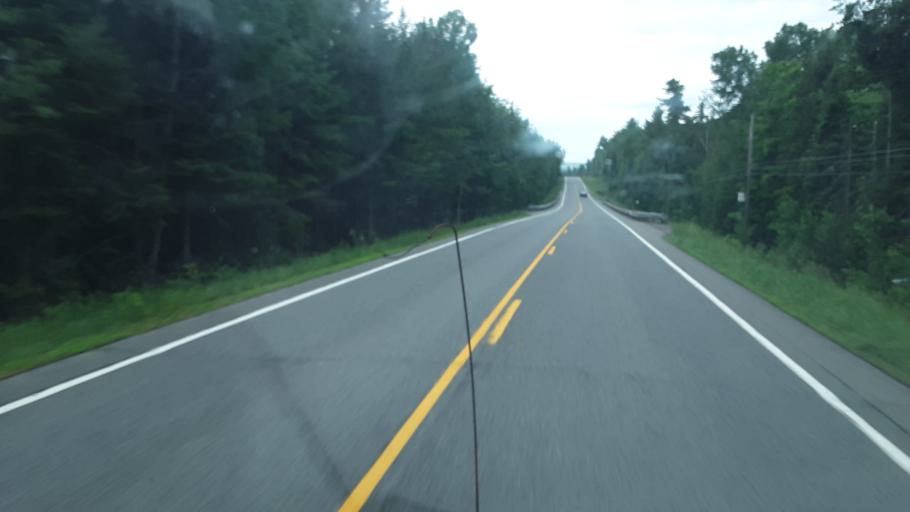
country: US
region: Maine
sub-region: Aroostook County
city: Presque Isle
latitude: 46.4534
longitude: -68.3845
